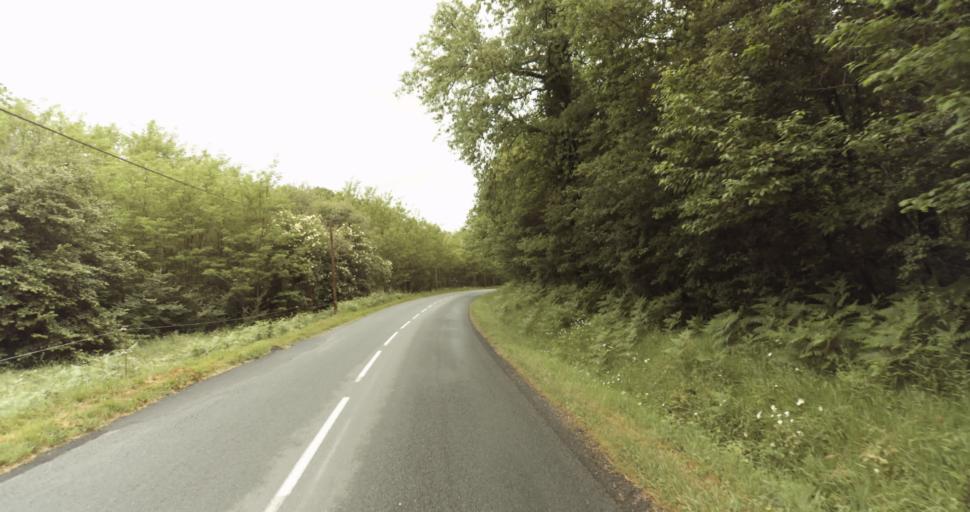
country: FR
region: Aquitaine
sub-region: Departement de la Dordogne
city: Belves
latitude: 44.7111
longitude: 0.9339
